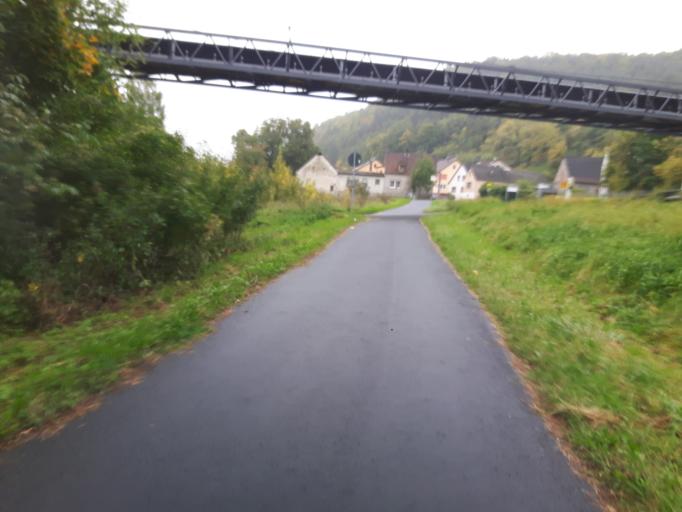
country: DE
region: Bavaria
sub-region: Regierungsbezirk Unterfranken
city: Karlstadt
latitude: 49.9523
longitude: 9.7623
